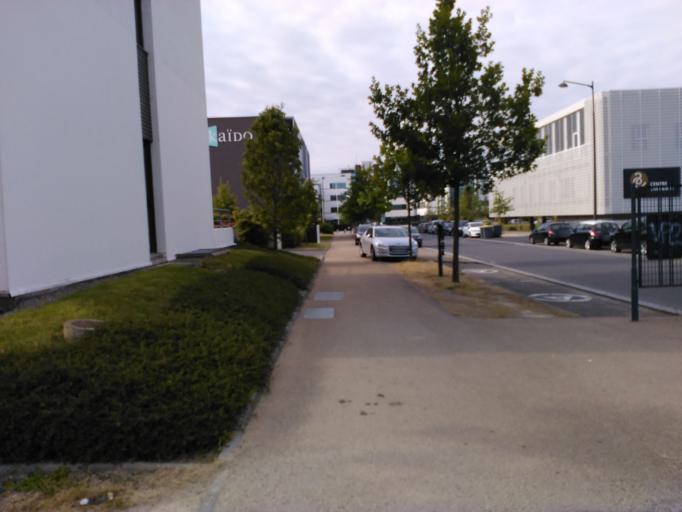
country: FR
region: Brittany
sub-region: Departement d'Ille-et-Vilaine
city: Rennes
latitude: 48.1158
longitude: -1.7137
